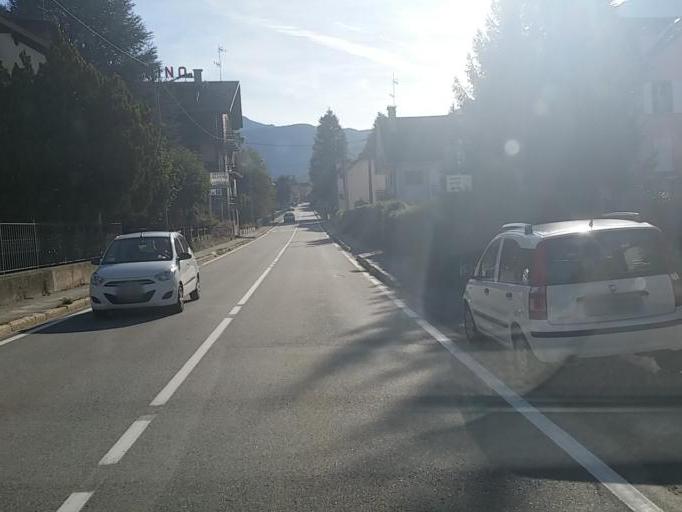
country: IT
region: Piedmont
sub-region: Provincia Verbano-Cusio-Ossola
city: Malesco
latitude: 46.1285
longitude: 8.4945
